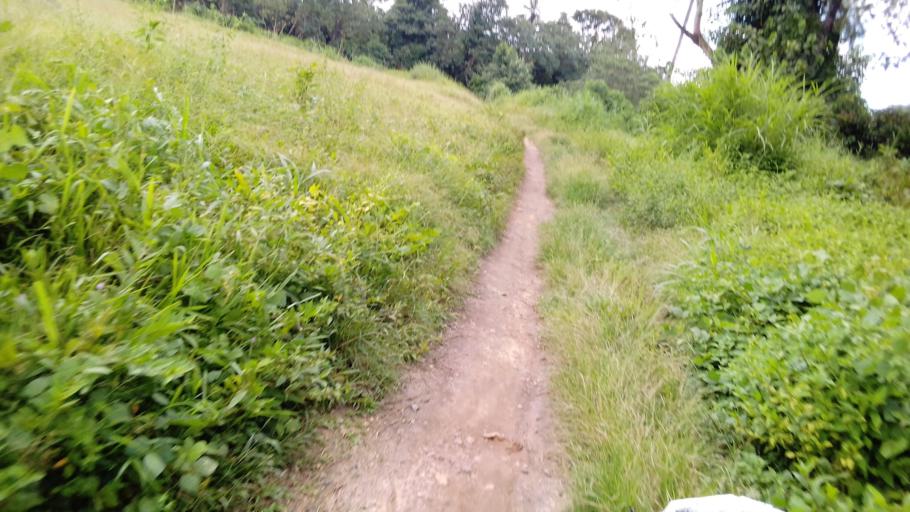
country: SL
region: Eastern Province
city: Koidu
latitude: 8.6787
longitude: -10.9765
